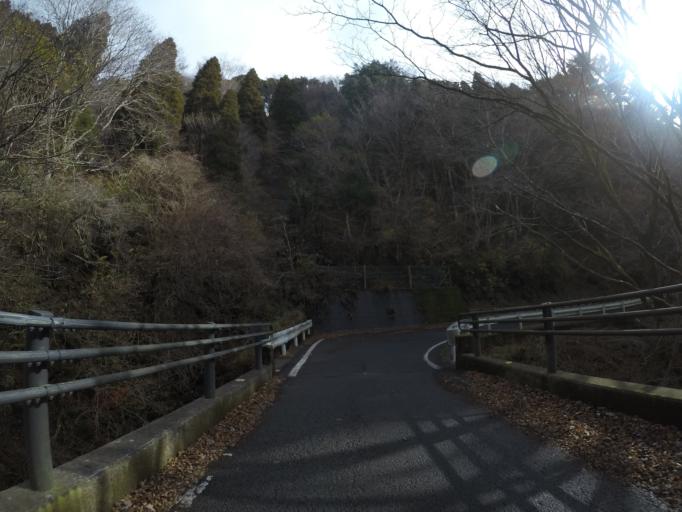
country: JP
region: Shizuoka
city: Heda
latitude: 34.8465
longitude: 138.8536
